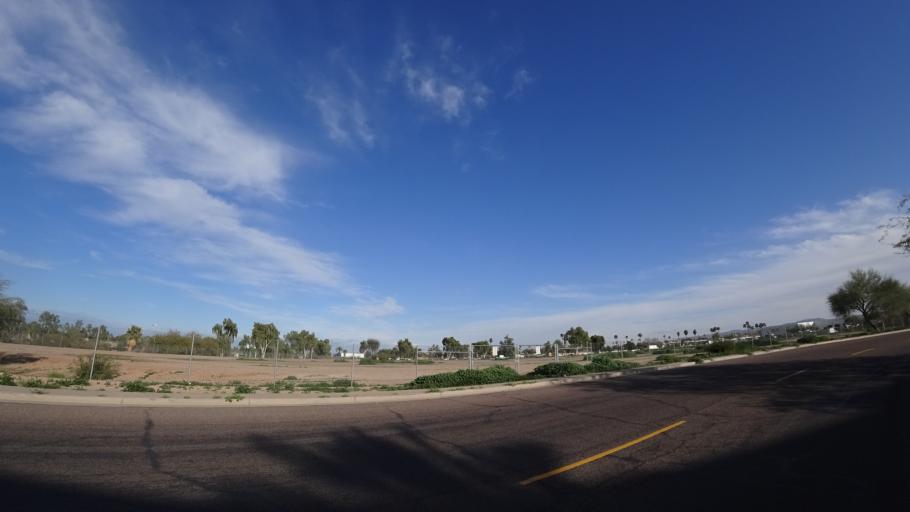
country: US
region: Arizona
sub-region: Maricopa County
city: Phoenix
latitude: 33.4610
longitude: -112.1547
